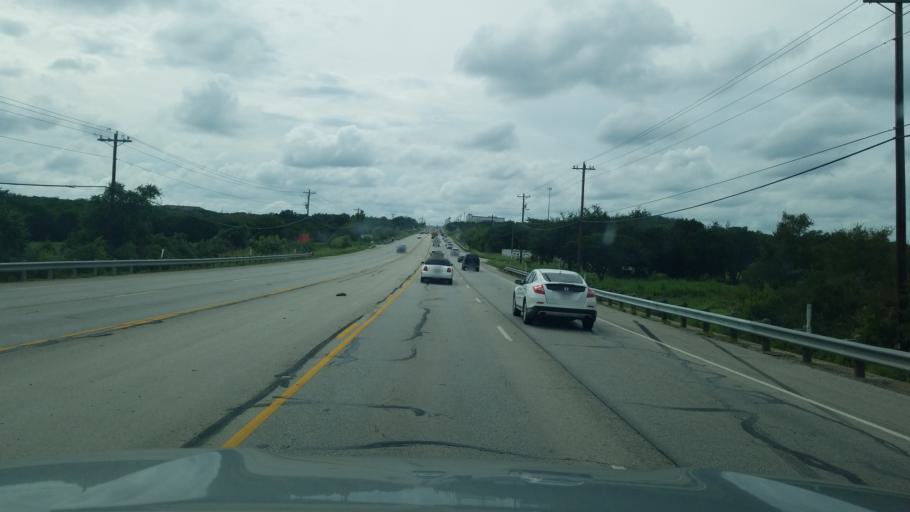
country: US
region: Texas
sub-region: Travis County
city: Barton Creek
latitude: 30.2344
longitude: -97.9211
